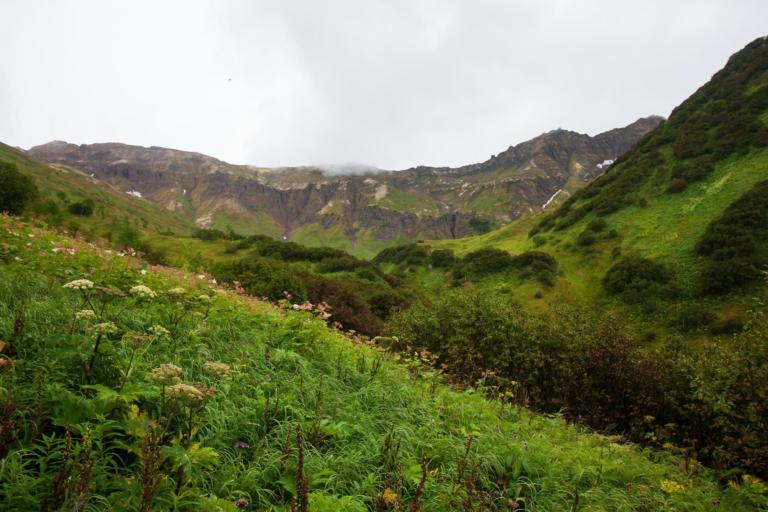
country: RU
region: Kamtsjatka
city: Yelizovo
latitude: 54.0255
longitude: 158.0785
